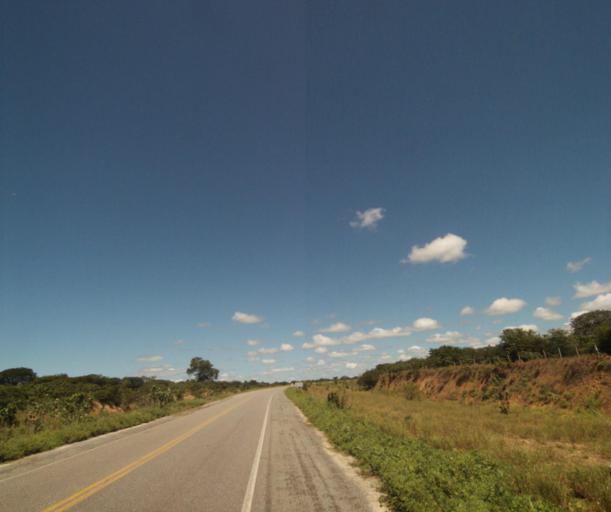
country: BR
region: Bahia
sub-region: Carinhanha
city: Carinhanha
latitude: -14.3187
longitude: -43.7815
